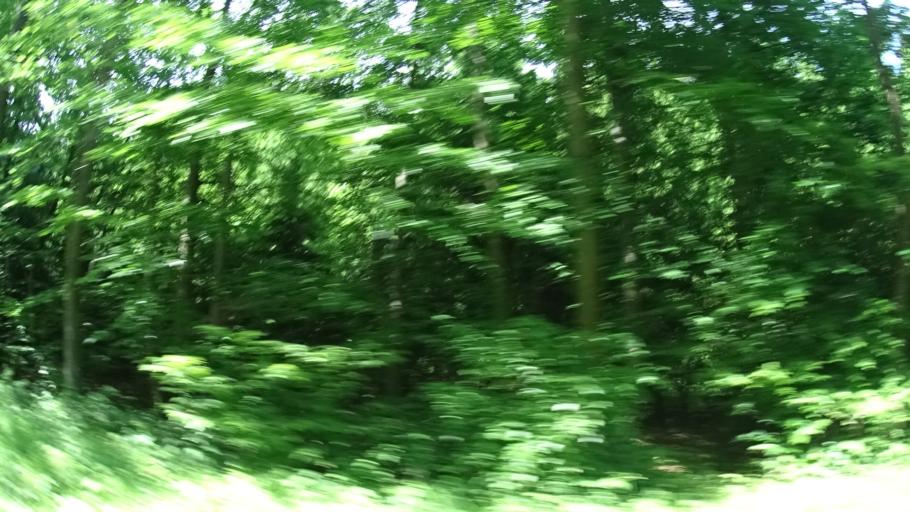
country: DE
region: Bavaria
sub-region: Regierungsbezirk Unterfranken
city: Greussenheim
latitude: 49.8767
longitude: 9.7554
